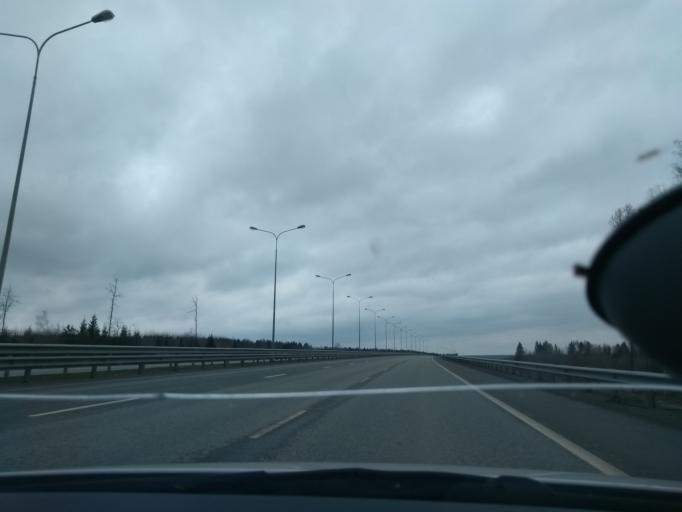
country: RU
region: Perm
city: Bershet'
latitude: 57.7036
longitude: 56.3729
